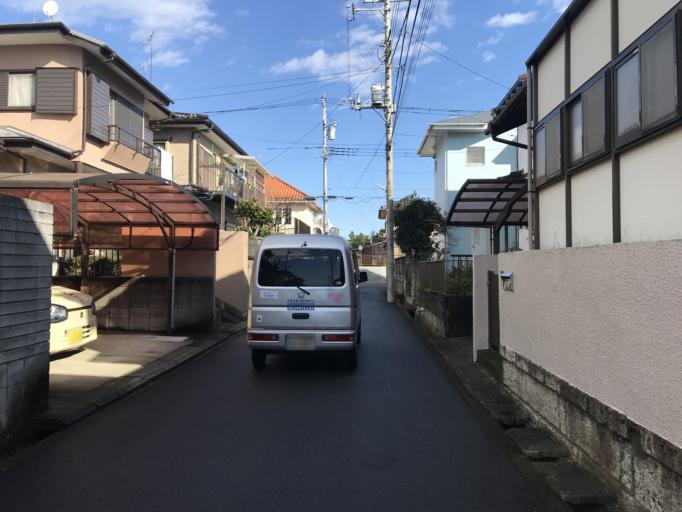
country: JP
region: Ibaraki
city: Ushiku
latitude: 35.9735
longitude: 140.1522
